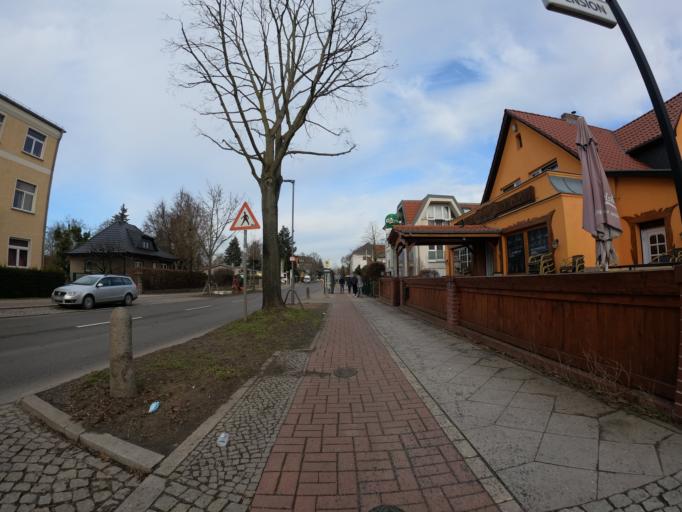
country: DE
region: Berlin
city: Mahlsdorf
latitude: 52.5200
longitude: 13.6174
